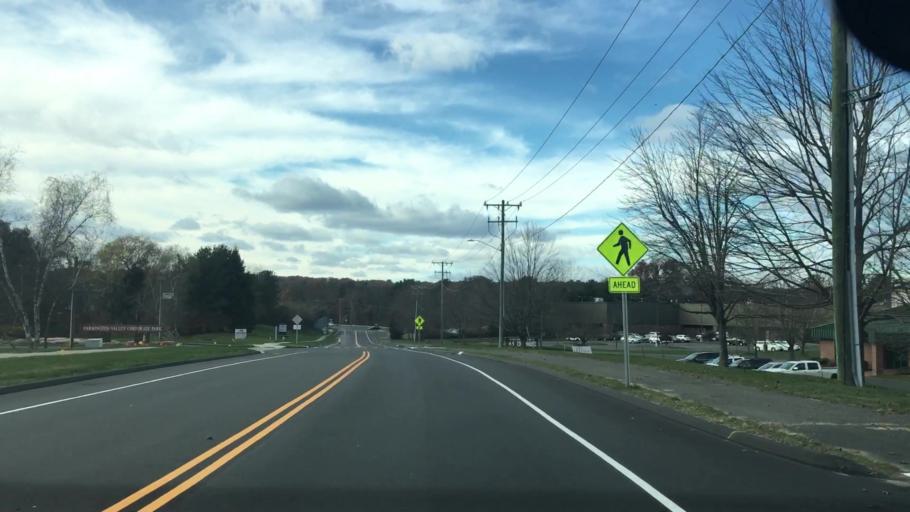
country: US
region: Connecticut
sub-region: Hartford County
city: Plainville
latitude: 41.6943
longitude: -72.8599
